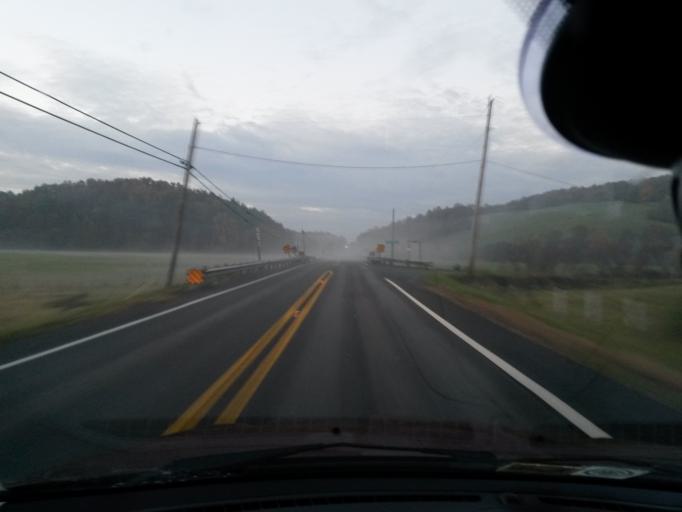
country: US
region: Virginia
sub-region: Alleghany County
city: Clifton Forge
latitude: 37.7478
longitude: -79.7906
